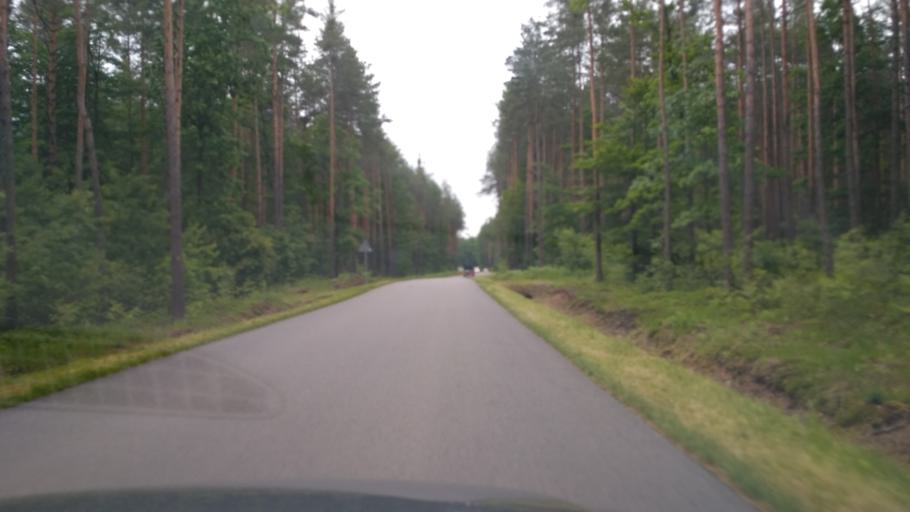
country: PL
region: Subcarpathian Voivodeship
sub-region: Powiat kolbuszowski
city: Niwiska
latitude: 50.1954
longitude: 21.6561
